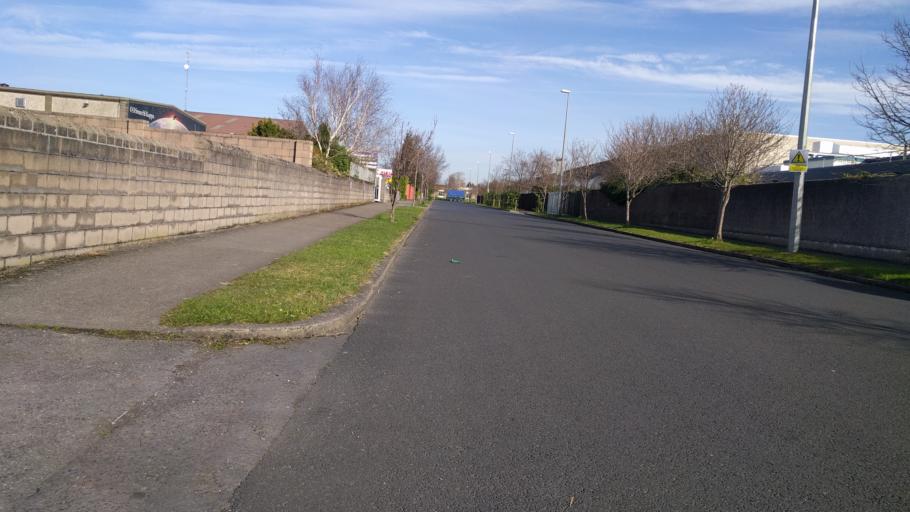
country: IE
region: Leinster
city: Tallaght
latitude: 53.2799
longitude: -6.3815
